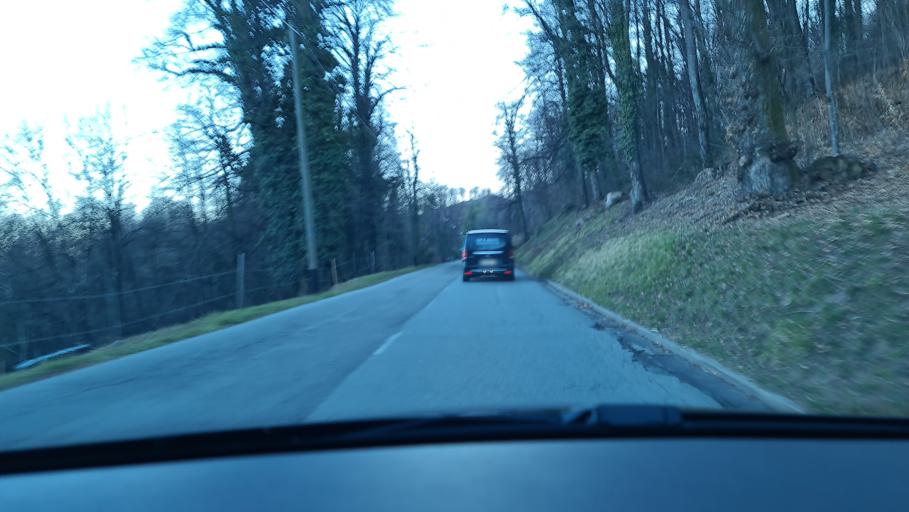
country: CH
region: Ticino
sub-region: Lugano District
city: Pura
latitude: 46.0312
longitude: 8.8590
